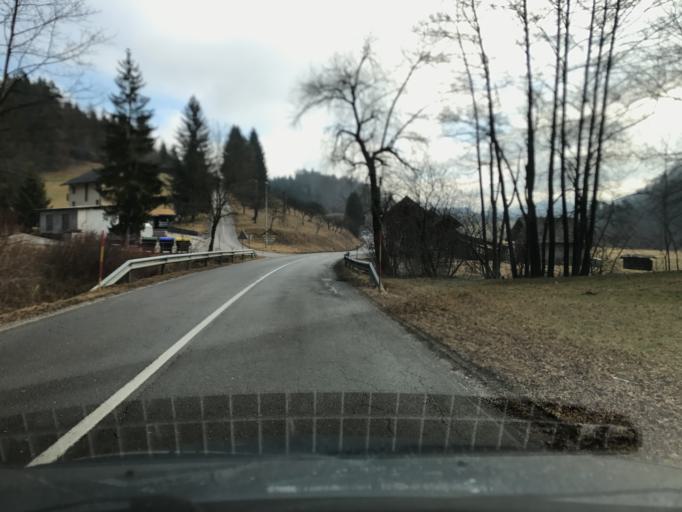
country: SI
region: Lukovica
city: Lukovica pri Domzalah
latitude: 46.2180
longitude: 14.7044
